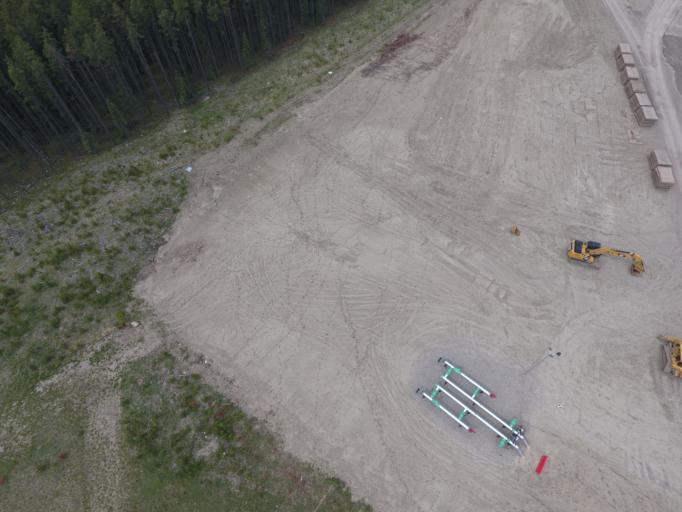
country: CA
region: Alberta
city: Edson
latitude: 52.8399
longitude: -116.0387
